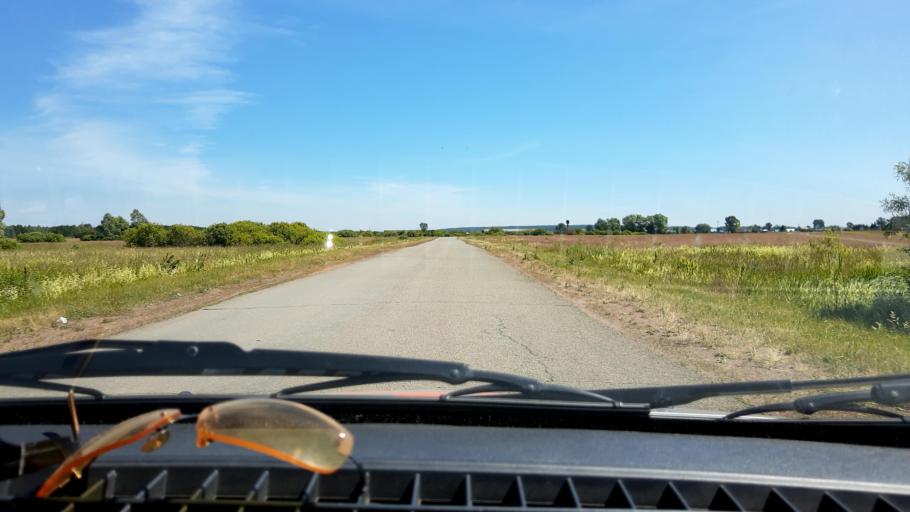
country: RU
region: Bashkortostan
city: Mikhaylovka
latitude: 54.9767
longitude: 55.7770
